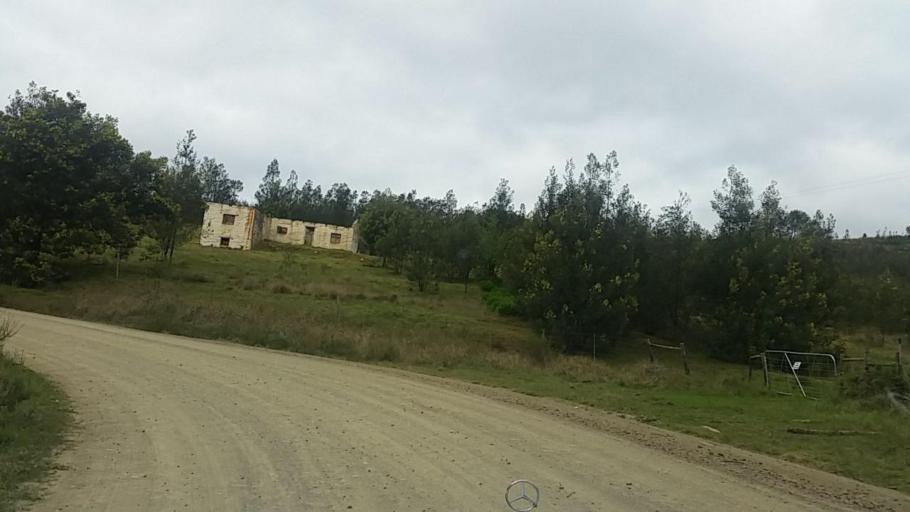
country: ZA
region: Western Cape
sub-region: Eden District Municipality
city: Knysna
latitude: -33.7476
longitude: 23.1689
